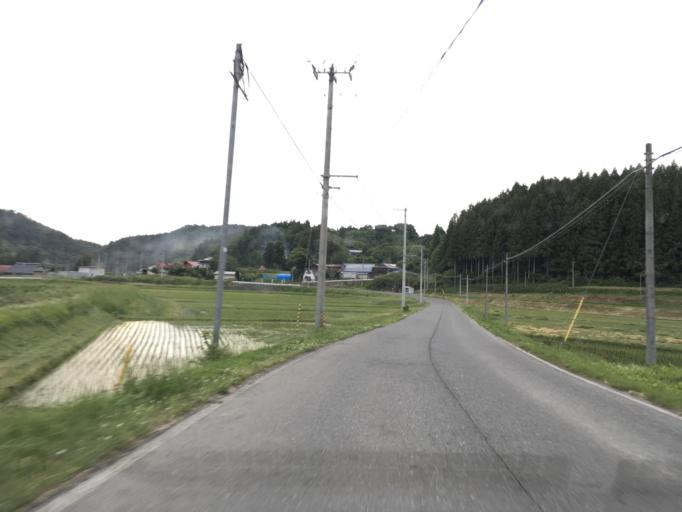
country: JP
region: Iwate
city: Mizusawa
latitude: 39.1726
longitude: 141.2972
